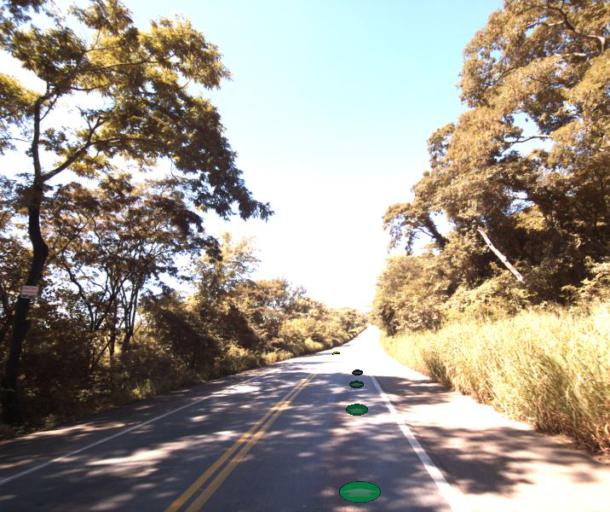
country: BR
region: Goias
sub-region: Jaragua
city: Jaragua
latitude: -15.5847
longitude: -49.4121
